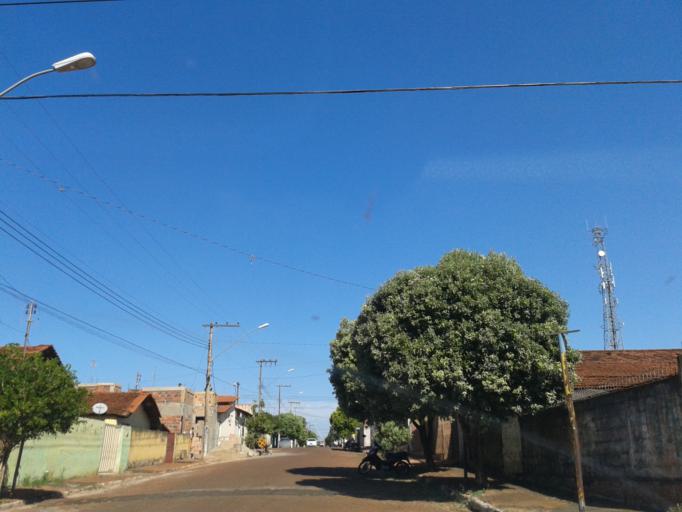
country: BR
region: Minas Gerais
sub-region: Centralina
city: Centralina
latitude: -18.5843
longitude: -49.1972
